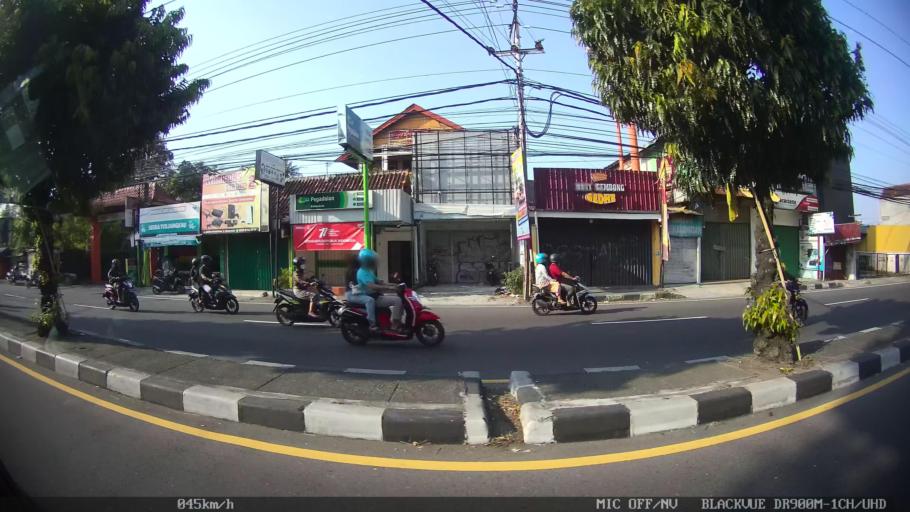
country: ID
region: Daerah Istimewa Yogyakarta
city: Depok
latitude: -7.7832
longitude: 110.4031
